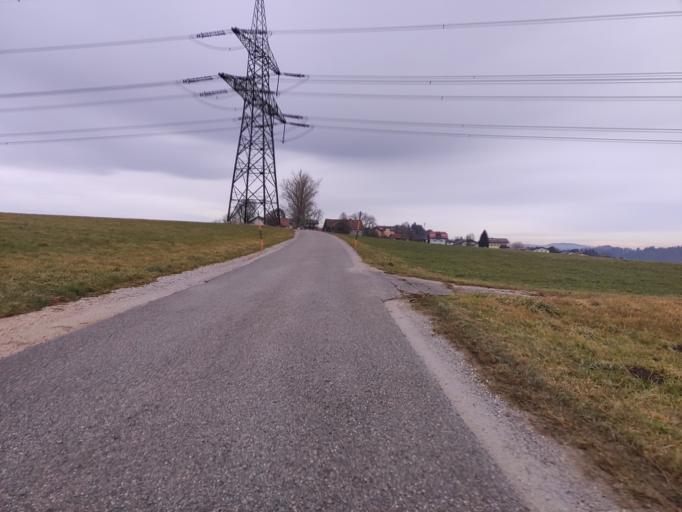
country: AT
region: Salzburg
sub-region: Politischer Bezirk Salzburg-Umgebung
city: Elixhausen
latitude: 47.9004
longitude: 13.0579
